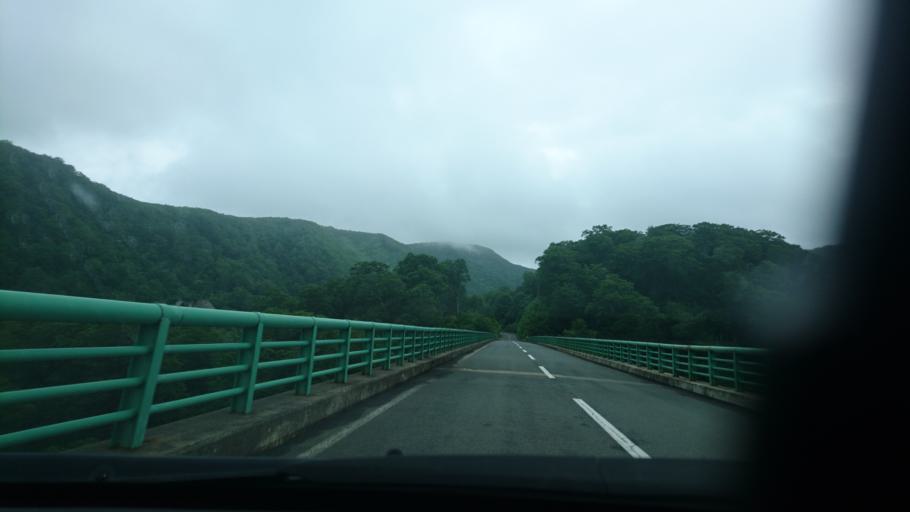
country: JP
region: Akita
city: Yuzawa
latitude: 39.1463
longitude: 140.7677
